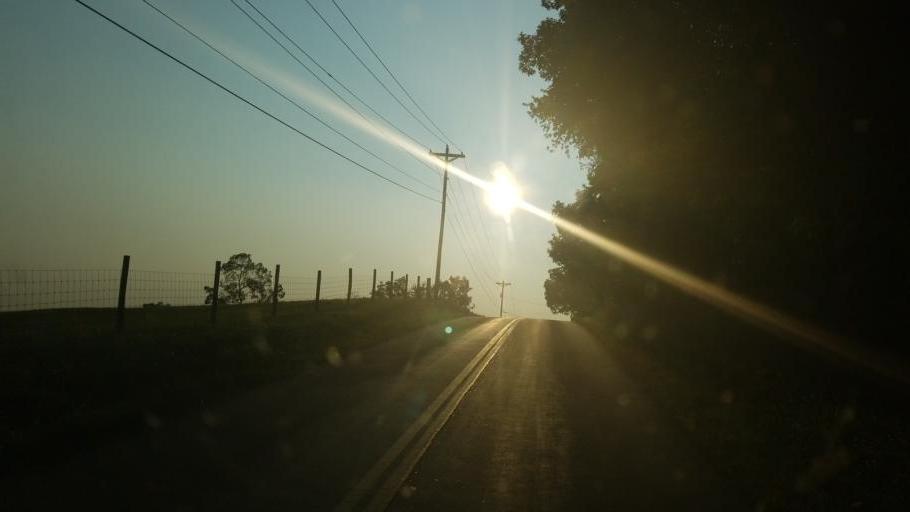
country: US
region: Ohio
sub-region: Wayne County
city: Shreve
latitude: 40.6710
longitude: -81.9285
